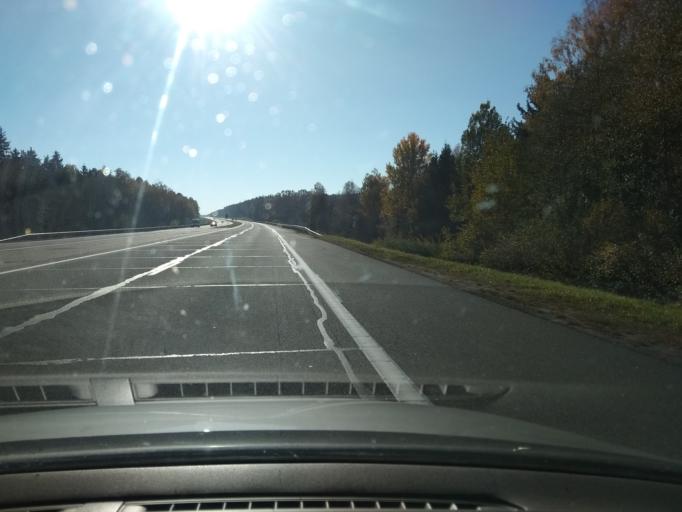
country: BY
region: Brest
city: Baranovichi
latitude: 53.0234
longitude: 25.7913
